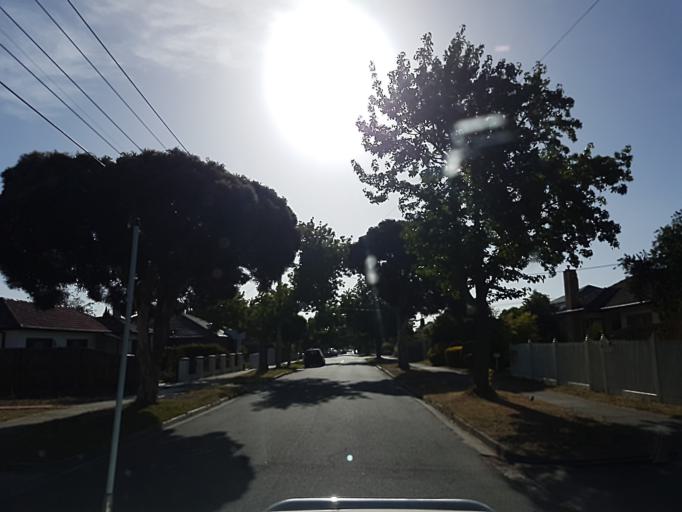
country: AU
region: Victoria
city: Clayton
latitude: -37.9084
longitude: 145.1083
